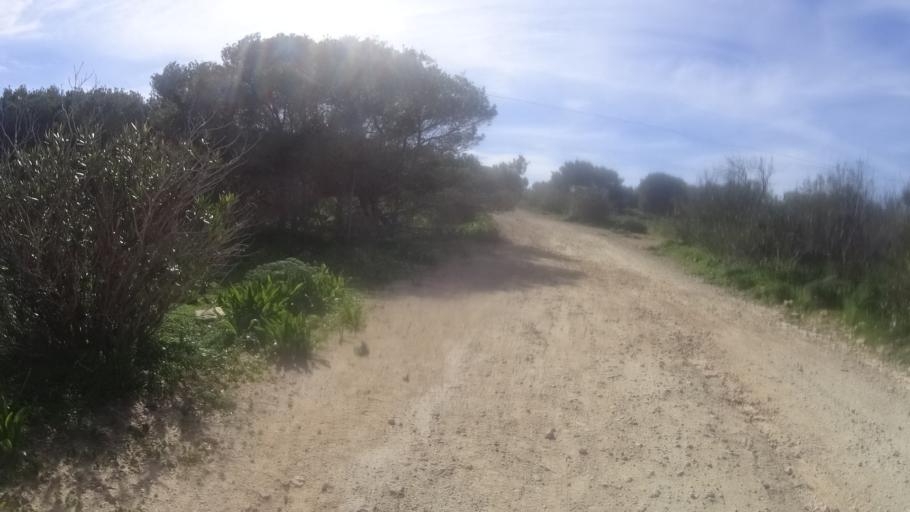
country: MT
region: Il-Qala
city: Qala
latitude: 36.0128
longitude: 14.3329
